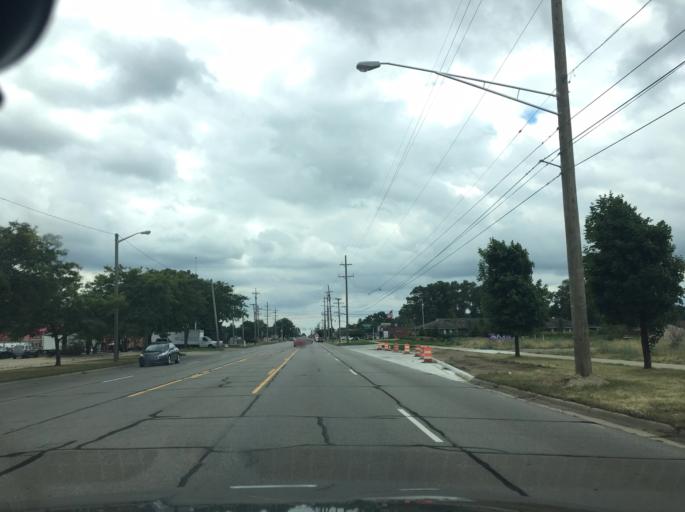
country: US
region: Michigan
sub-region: Macomb County
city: Shelby
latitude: 42.6582
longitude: -83.0336
